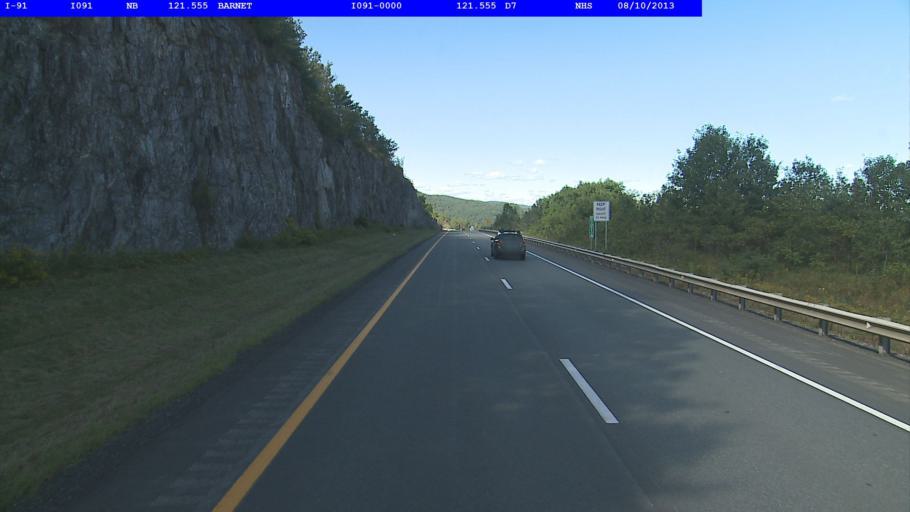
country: US
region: Vermont
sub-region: Caledonia County
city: Saint Johnsbury
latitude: 44.3047
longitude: -72.0379
